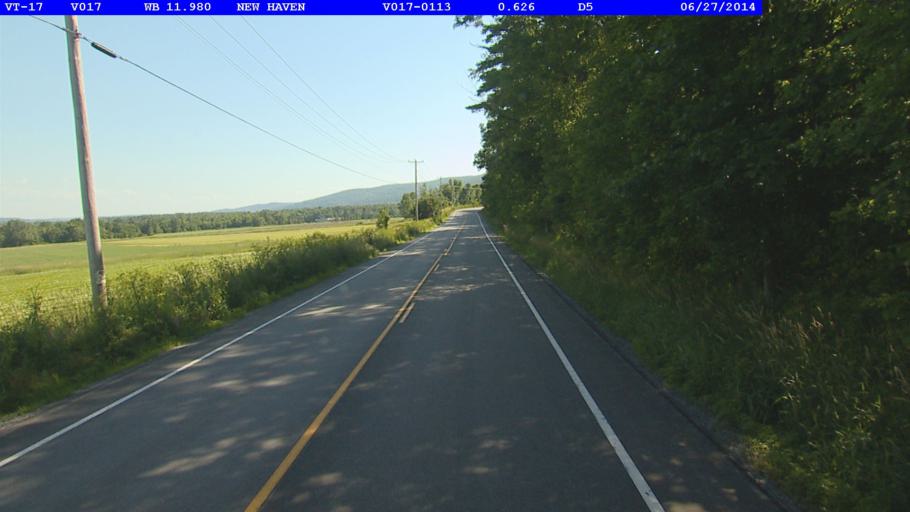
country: US
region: Vermont
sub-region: Addison County
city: Vergennes
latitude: 44.0894
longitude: -73.2355
